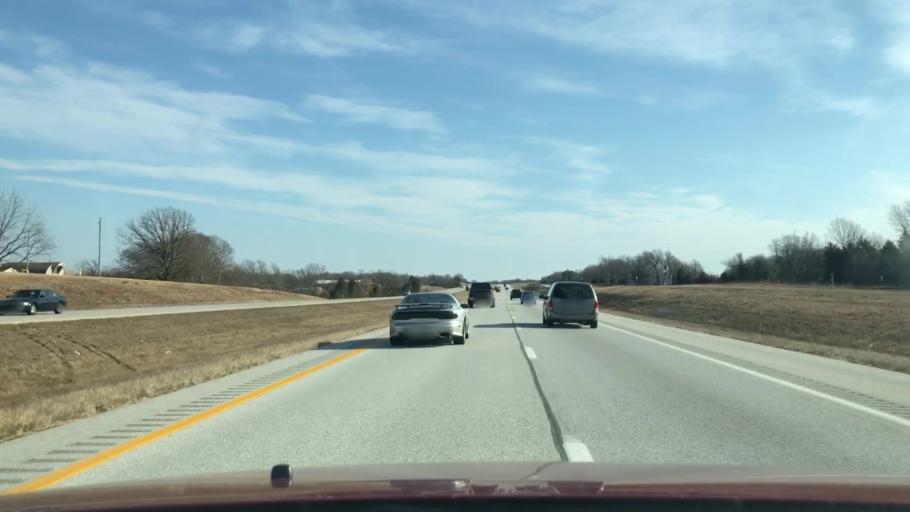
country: US
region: Missouri
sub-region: Webster County
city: Seymour
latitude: 37.1597
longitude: -92.9138
